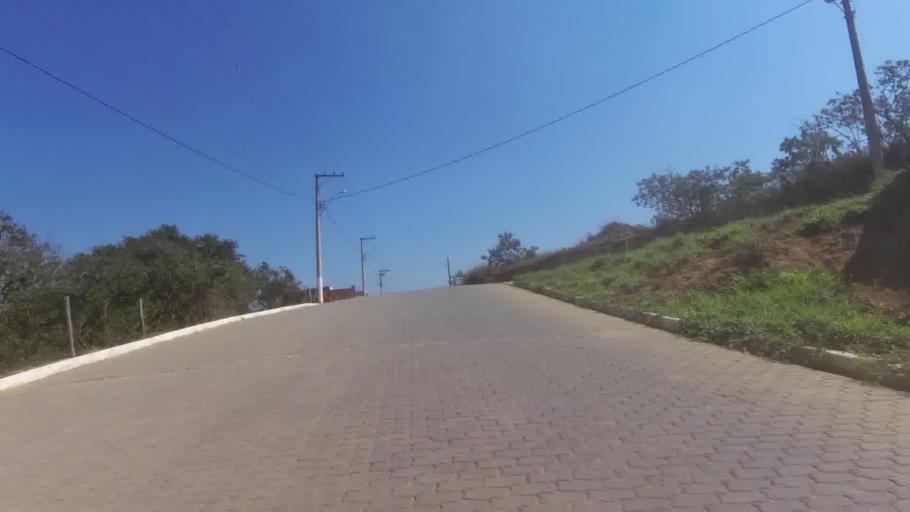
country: BR
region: Espirito Santo
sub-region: Itapemirim
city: Itapemirim
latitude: -21.0174
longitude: -40.8220
